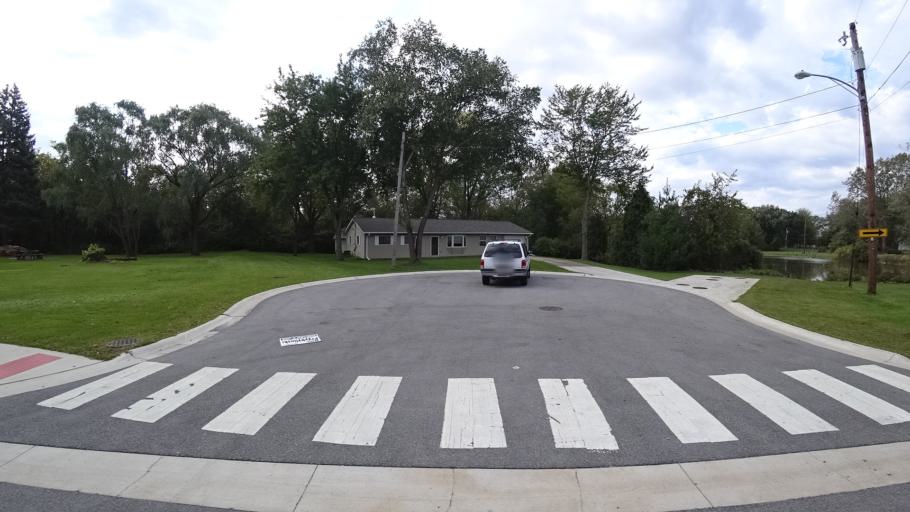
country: US
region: Indiana
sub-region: LaPorte County
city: Michigan City
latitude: 41.6717
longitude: -86.8972
